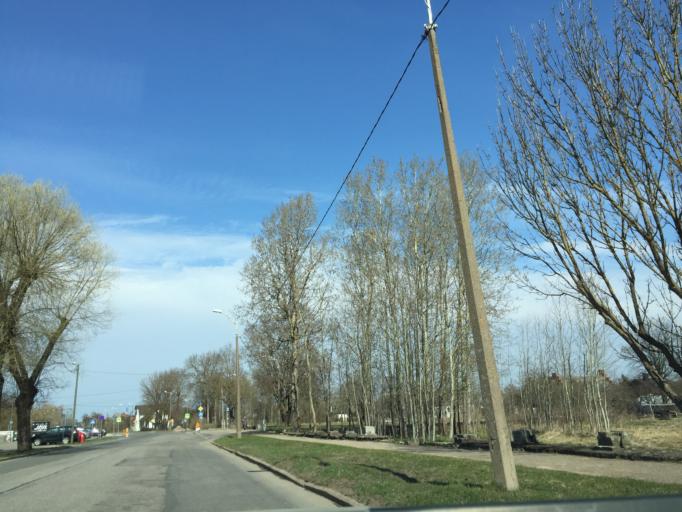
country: EE
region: Ida-Virumaa
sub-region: Narva linn
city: Narva
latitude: 59.3856
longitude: 28.1987
